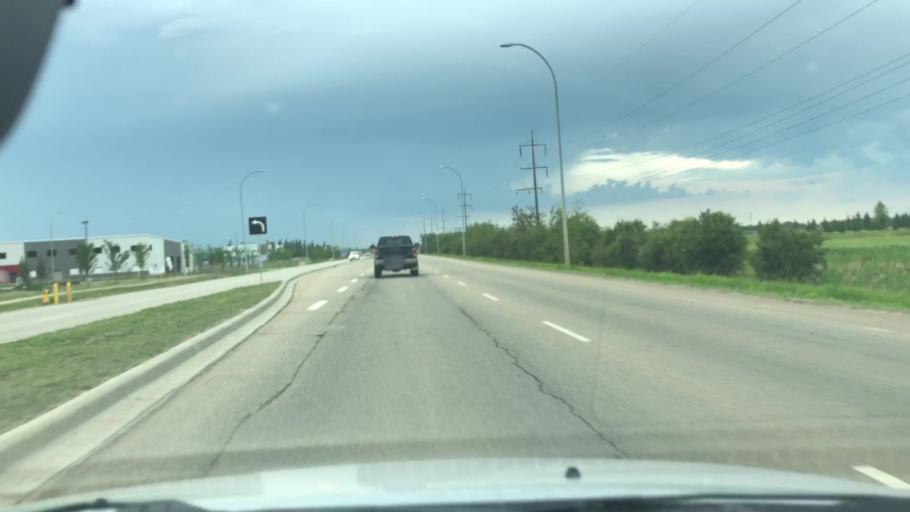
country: CA
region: Alberta
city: St. Albert
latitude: 53.5995
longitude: -113.5948
